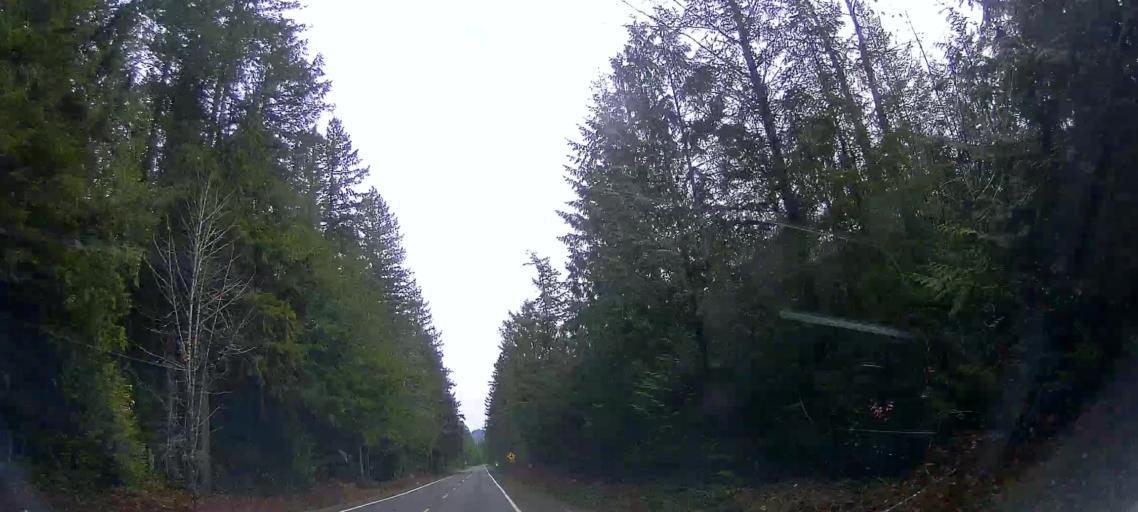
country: US
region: Washington
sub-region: Snohomish County
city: Darrington
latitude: 48.5271
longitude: -121.8288
